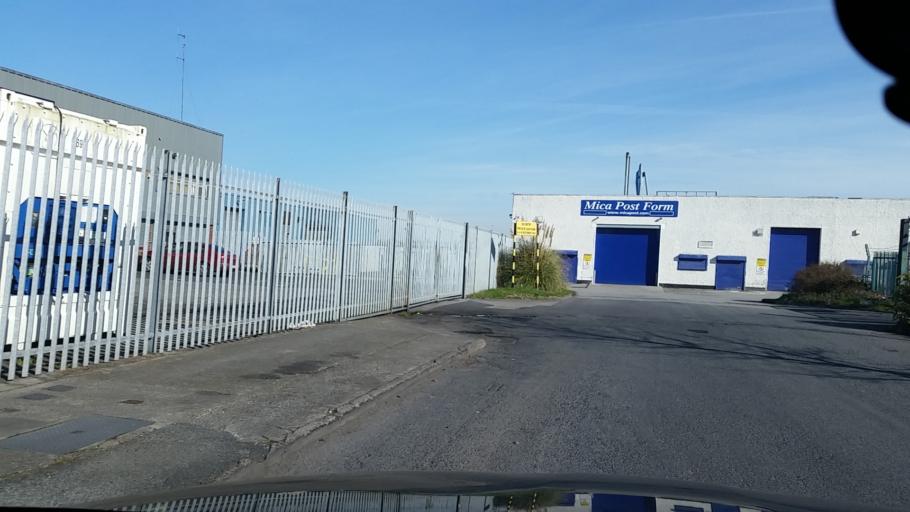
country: IE
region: Leinster
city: Ballymun
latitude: 53.4015
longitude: -6.2696
